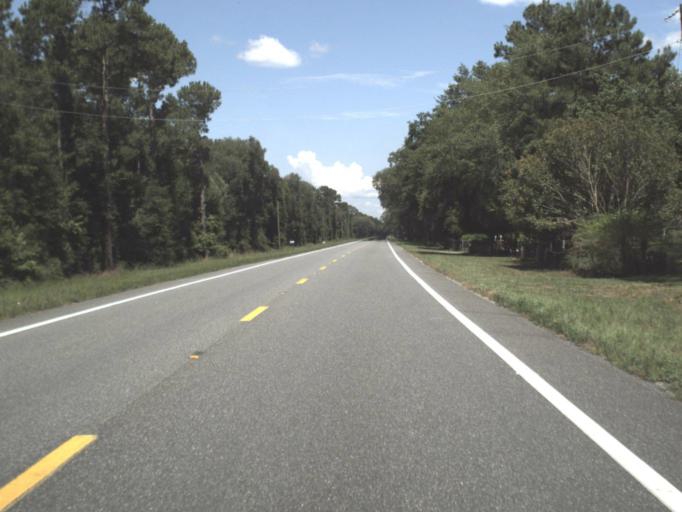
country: US
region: Florida
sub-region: Lafayette County
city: Mayo
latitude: 30.1294
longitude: -83.3305
